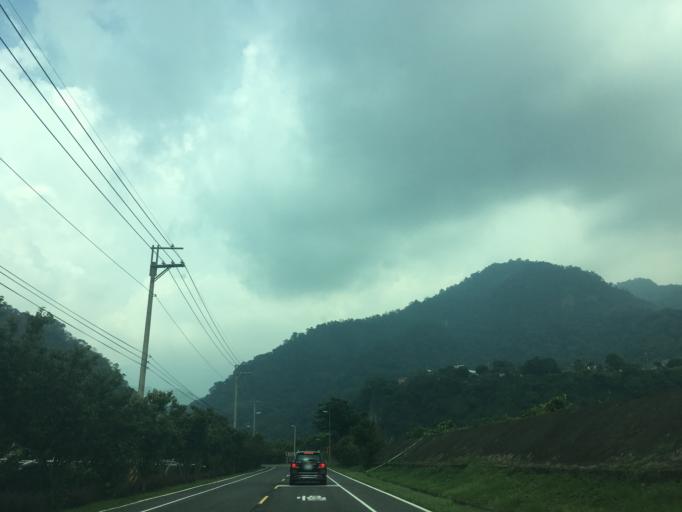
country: TW
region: Taiwan
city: Fengyuan
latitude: 24.2941
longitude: 120.9038
